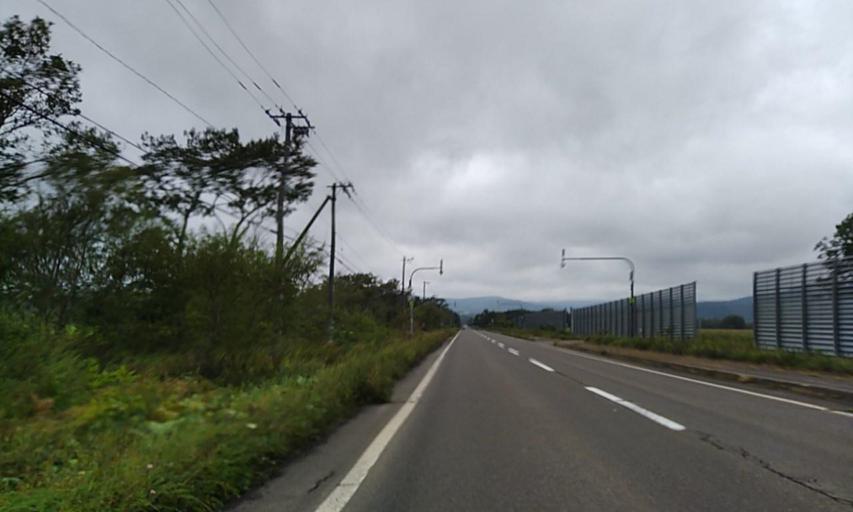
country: JP
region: Hokkaido
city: Bihoro
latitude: 43.5092
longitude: 144.4665
